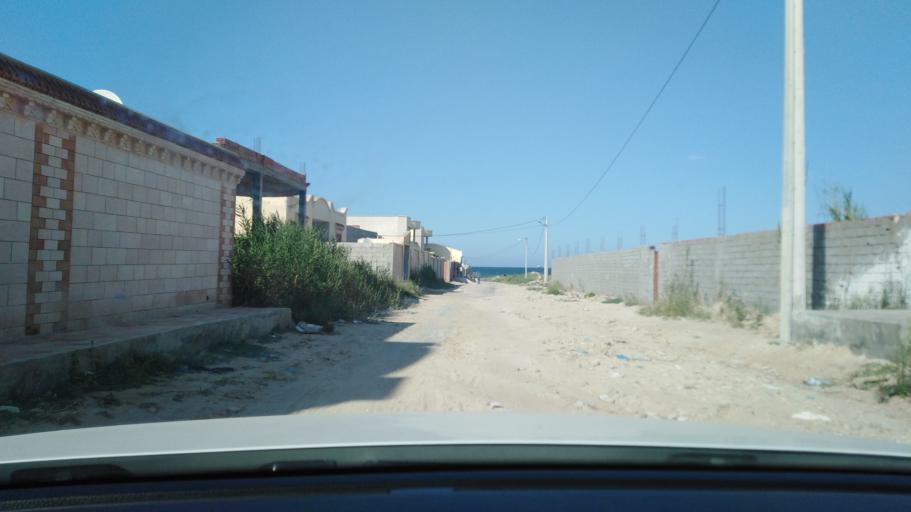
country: TN
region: Qabis
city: Gabes
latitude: 33.9431
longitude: 10.0752
